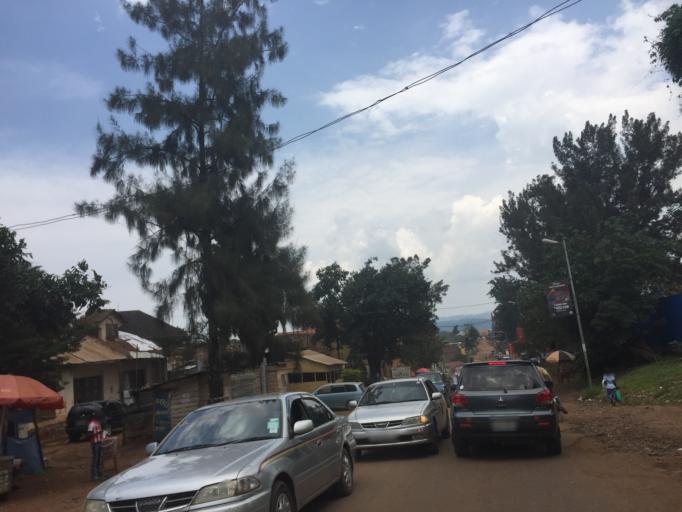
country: CD
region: South Kivu
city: Bukavu
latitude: -2.4870
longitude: 28.8571
